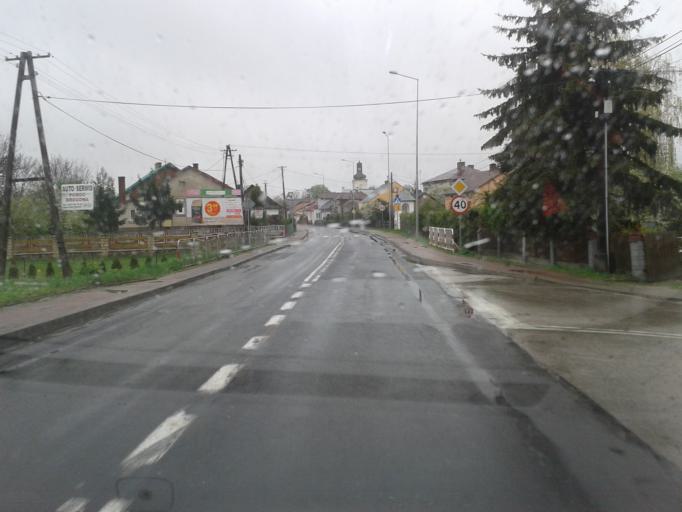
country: PL
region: Subcarpathian Voivodeship
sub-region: Powiat lubaczowski
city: Narol
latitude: 50.3521
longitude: 23.3275
